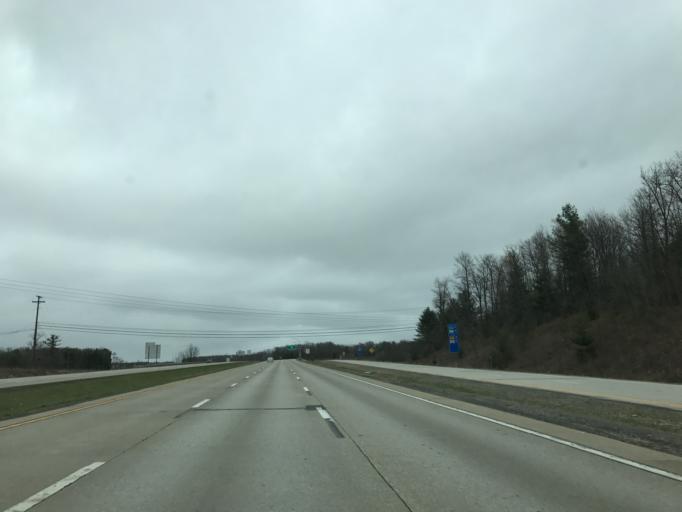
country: US
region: West Virginia
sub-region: Raleigh County
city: Beaver
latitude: 37.7662
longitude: -81.1305
